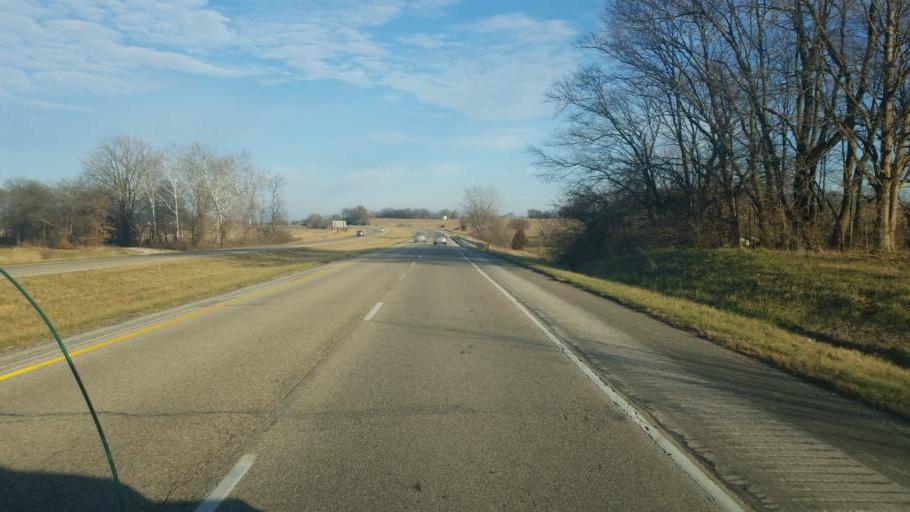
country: US
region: Indiana
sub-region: Knox County
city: Vincennes
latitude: 38.6753
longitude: -87.4320
